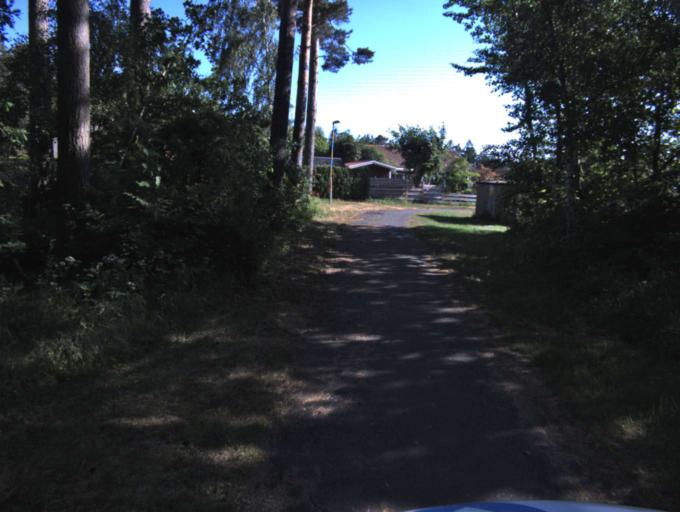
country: SE
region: Skane
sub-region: Kristianstads Kommun
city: Fjalkinge
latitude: 56.0473
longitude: 14.3322
